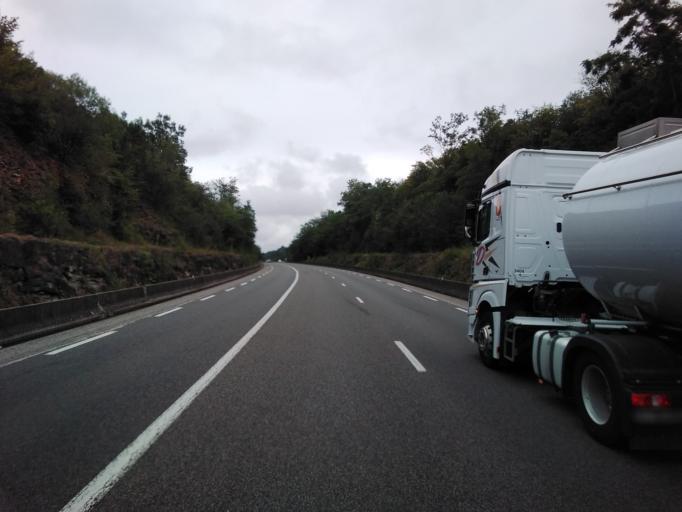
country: FR
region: Franche-Comte
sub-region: Departement de la Haute-Saone
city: Echenoz-la-Meline
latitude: 47.5898
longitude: 6.1098
